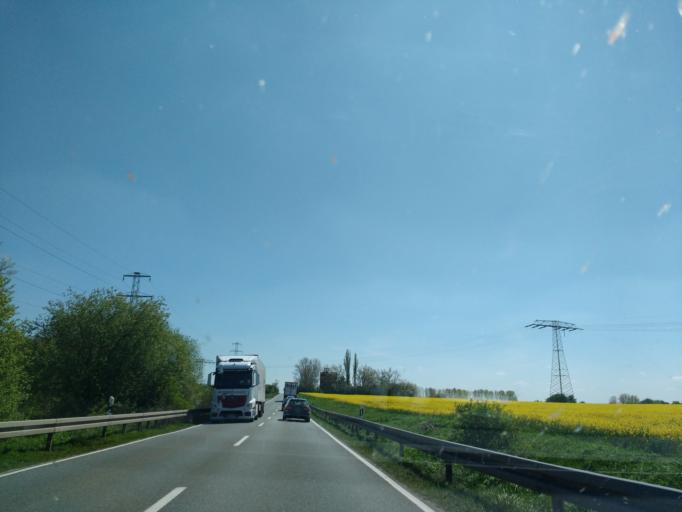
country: DE
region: Saxony-Anhalt
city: Deuben
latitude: 51.1052
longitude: 12.0923
